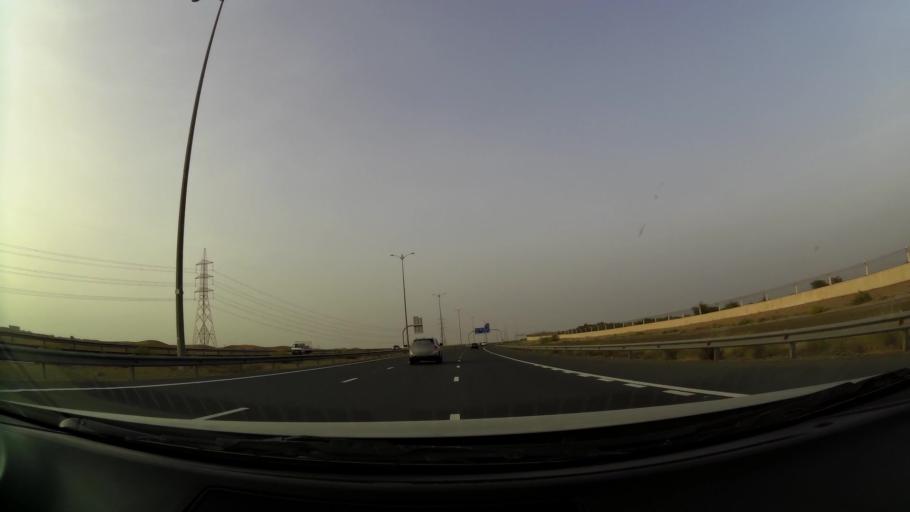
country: OM
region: Al Buraimi
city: Al Buraymi
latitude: 24.3282
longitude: 55.7599
